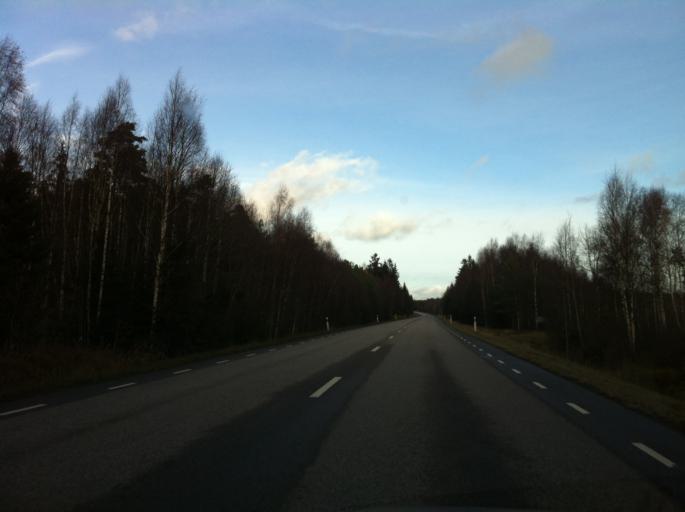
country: SE
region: Kronoberg
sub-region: Almhults Kommun
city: AElmhult
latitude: 56.5848
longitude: 14.1911
